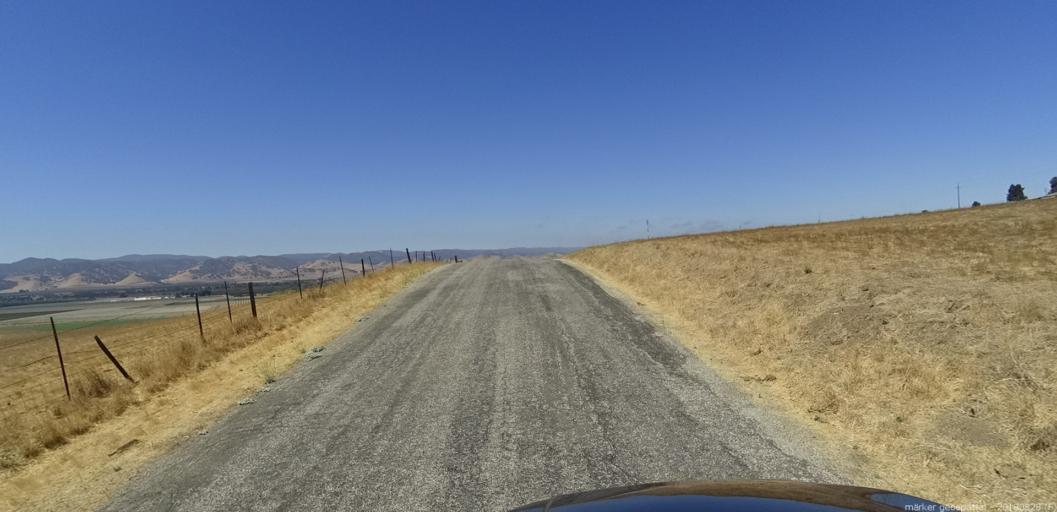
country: US
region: California
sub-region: San Luis Obispo County
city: Lake Nacimiento
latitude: 36.0235
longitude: -120.8849
